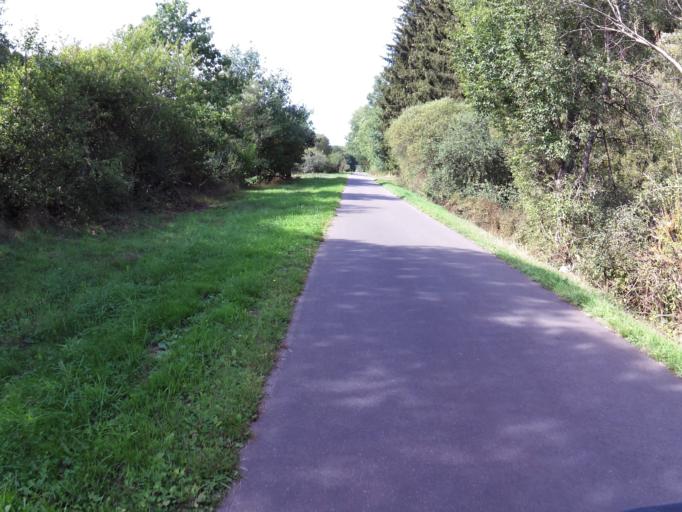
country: DE
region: Rheinland-Pfalz
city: Pronsfeld
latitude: 50.1830
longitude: 6.3128
